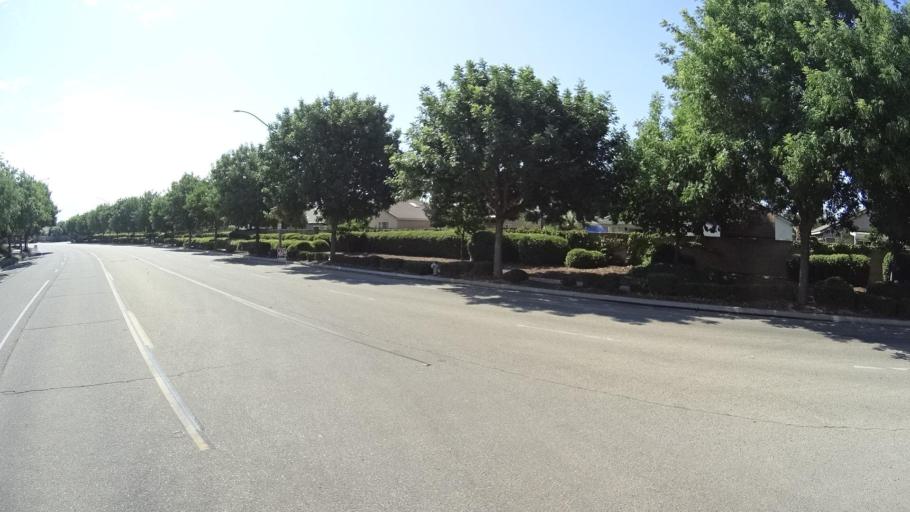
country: US
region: California
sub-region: Fresno County
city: Sunnyside
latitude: 36.7200
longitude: -119.6933
